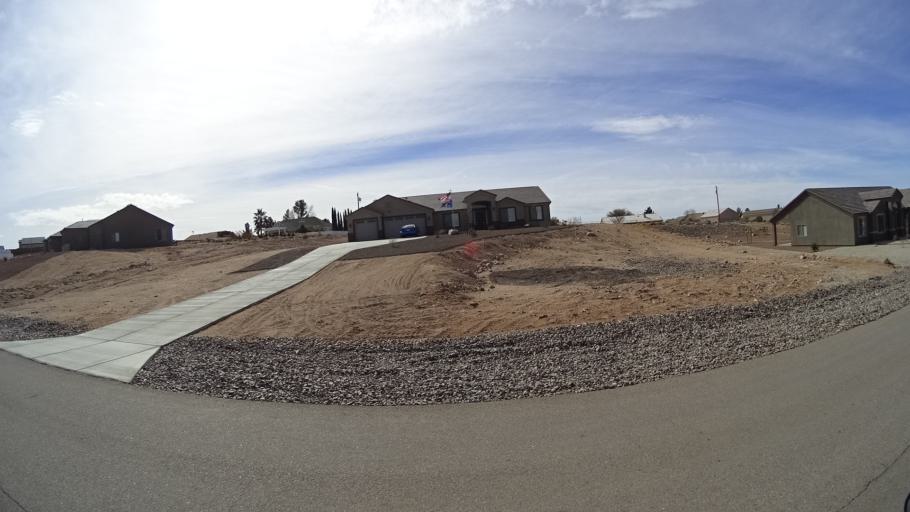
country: US
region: Arizona
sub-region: Mohave County
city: Kingman
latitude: 35.1855
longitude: -113.9790
